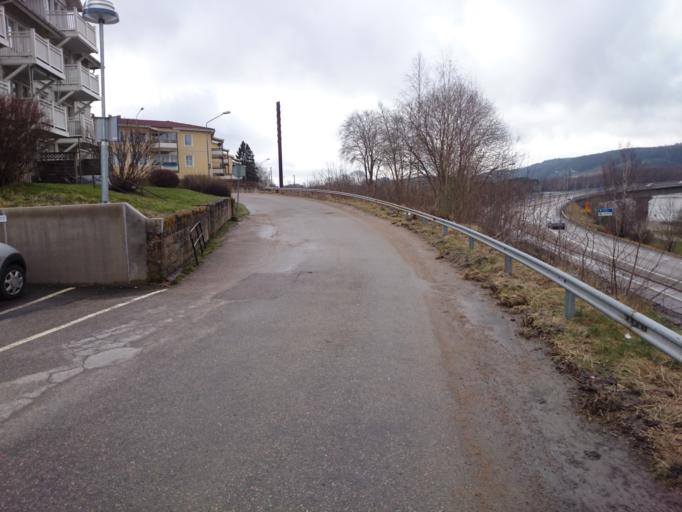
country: SE
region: Vaestra Goetaland
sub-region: Lilla Edets Kommun
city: Lilla Edet
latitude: 58.1354
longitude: 12.1223
